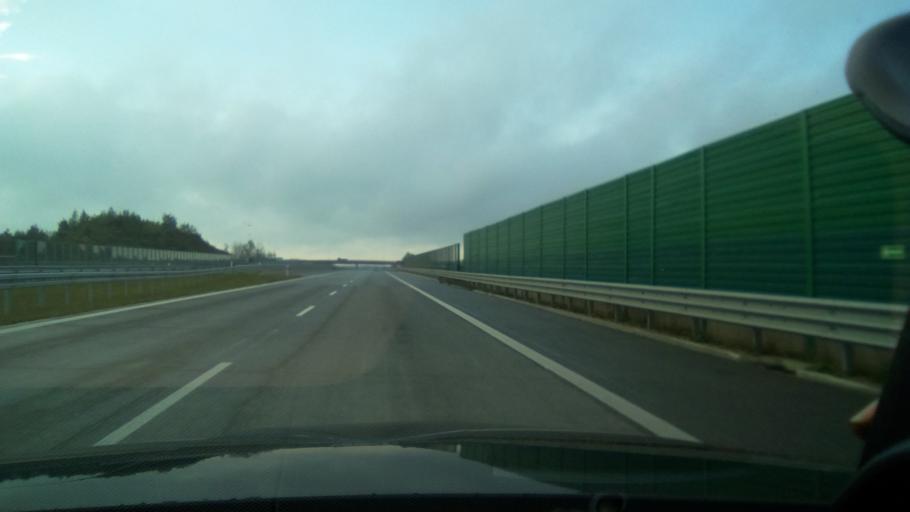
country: PL
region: Silesian Voivodeship
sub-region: Powiat czestochowski
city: Konopiska
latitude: 50.7662
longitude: 19.0163
